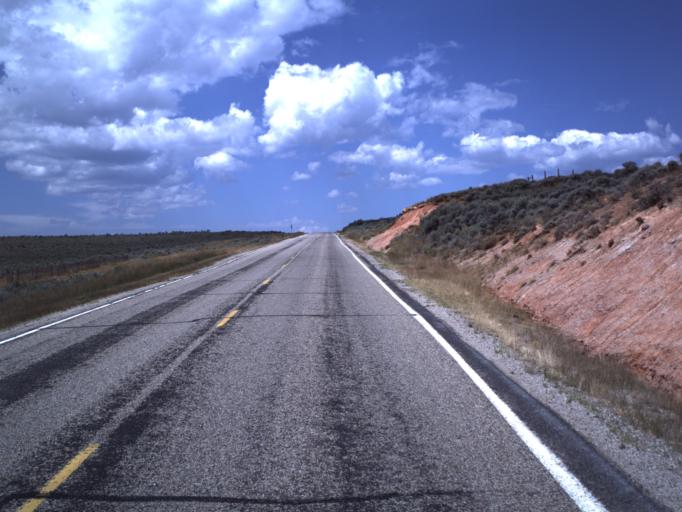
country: US
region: Utah
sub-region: Rich County
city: Randolph
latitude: 41.7973
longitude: -111.2363
